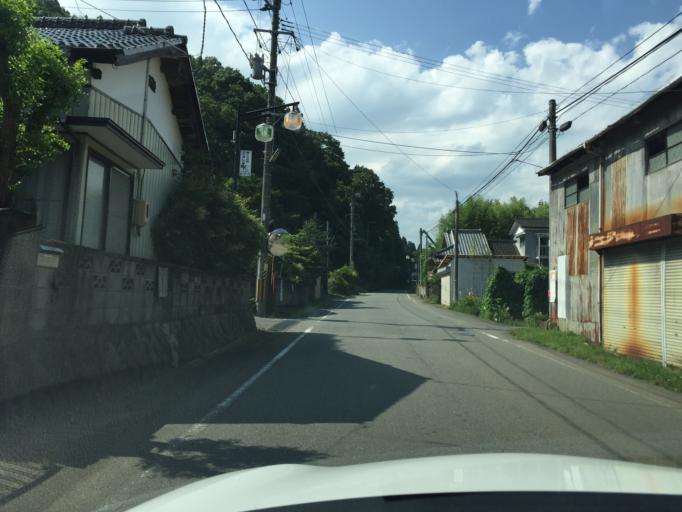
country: JP
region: Ibaraki
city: Kitaibaraki
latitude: 36.9698
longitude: 140.7045
